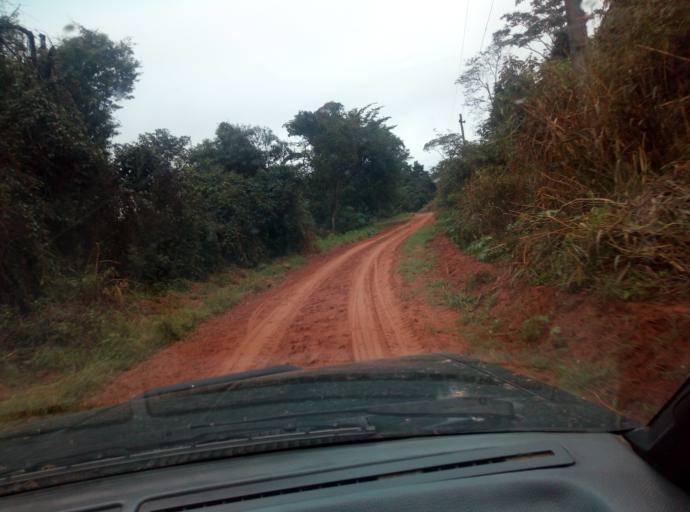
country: PY
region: Caaguazu
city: Carayao
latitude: -25.1914
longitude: -56.3444
